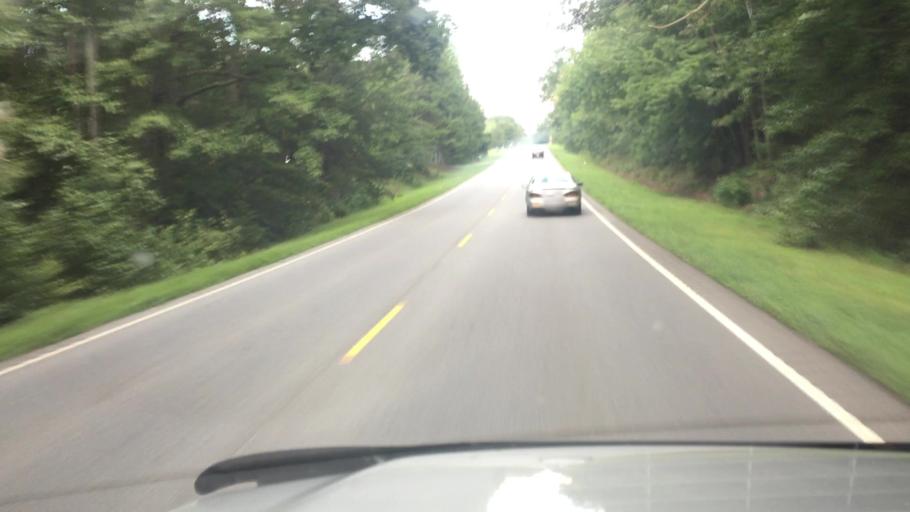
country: US
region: South Carolina
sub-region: Spartanburg County
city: Mayo
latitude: 35.1238
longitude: -81.7692
